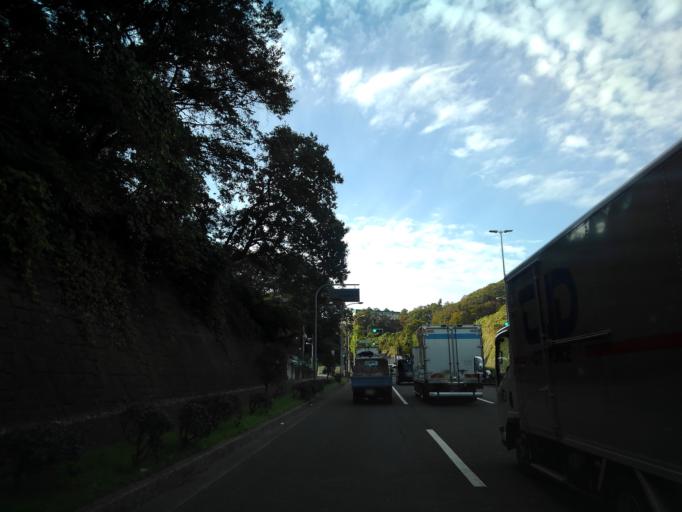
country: JP
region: Tokyo
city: Hachioji
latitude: 35.6913
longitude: 139.3483
